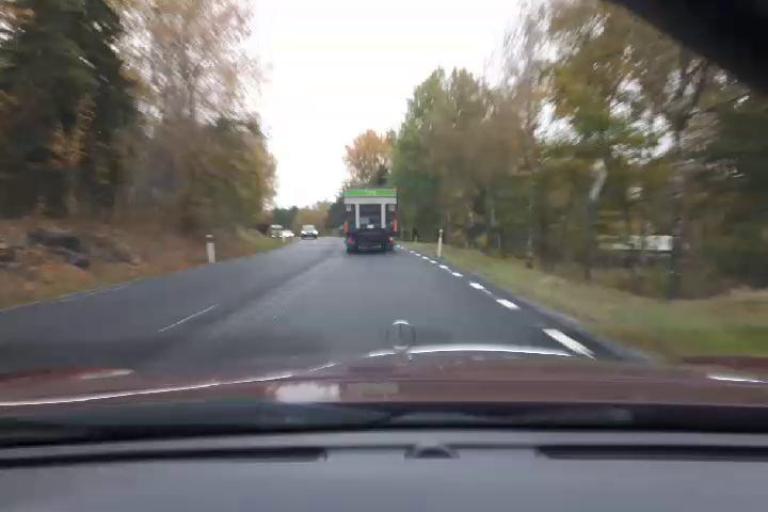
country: SE
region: Soedermanland
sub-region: Strangnas Kommun
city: Strangnas
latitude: 59.4243
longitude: 17.0255
